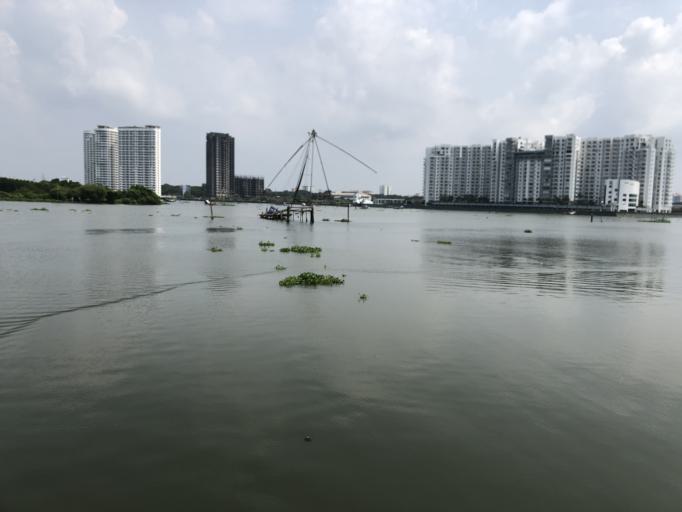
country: IN
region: Kerala
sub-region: Ernakulam
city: Cochin
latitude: 9.9963
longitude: 76.2657
